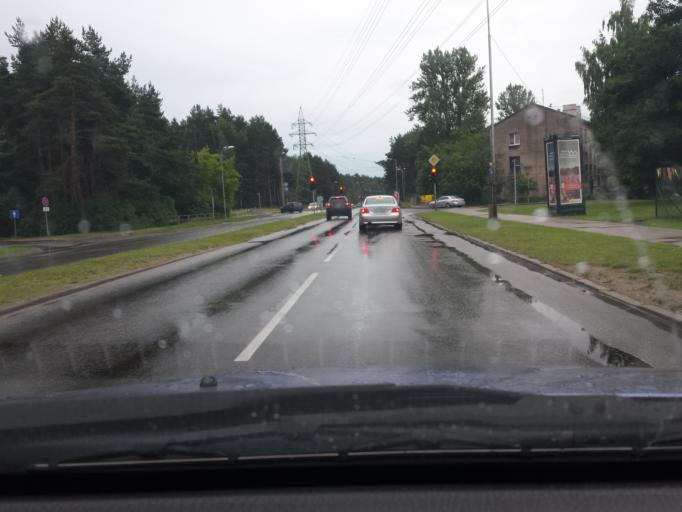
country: LV
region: Riga
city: Jaunciems
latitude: 56.9683
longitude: 24.1958
